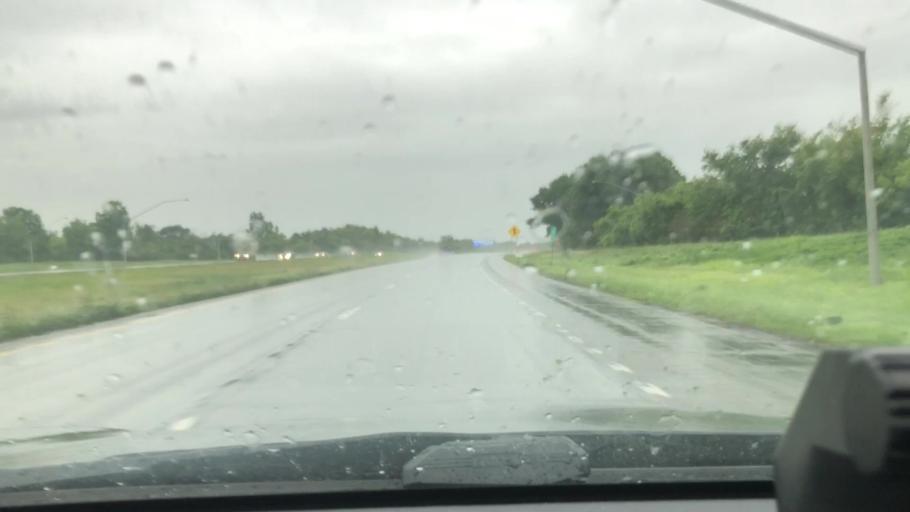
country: US
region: Pennsylvania
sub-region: Northampton County
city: Tatamy
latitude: 40.7546
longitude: -75.2680
